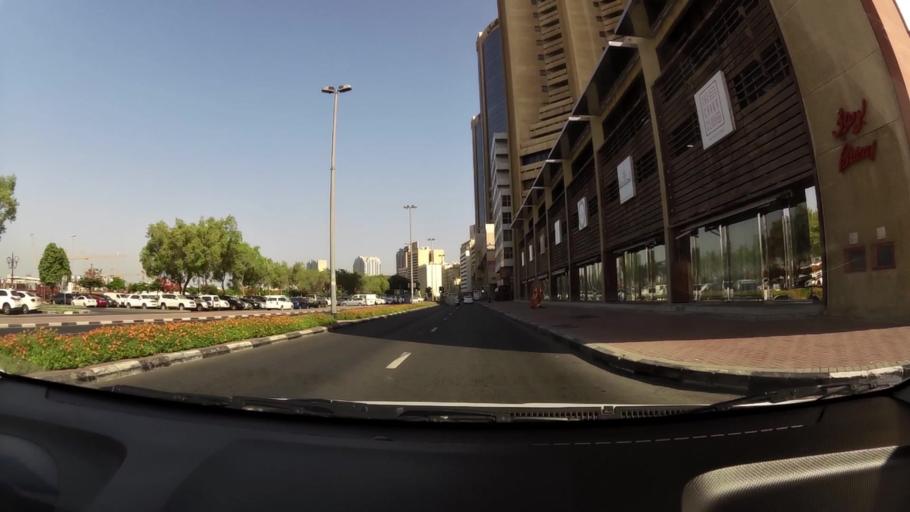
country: AE
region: Ash Shariqah
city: Sharjah
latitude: 25.2650
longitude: 55.3101
